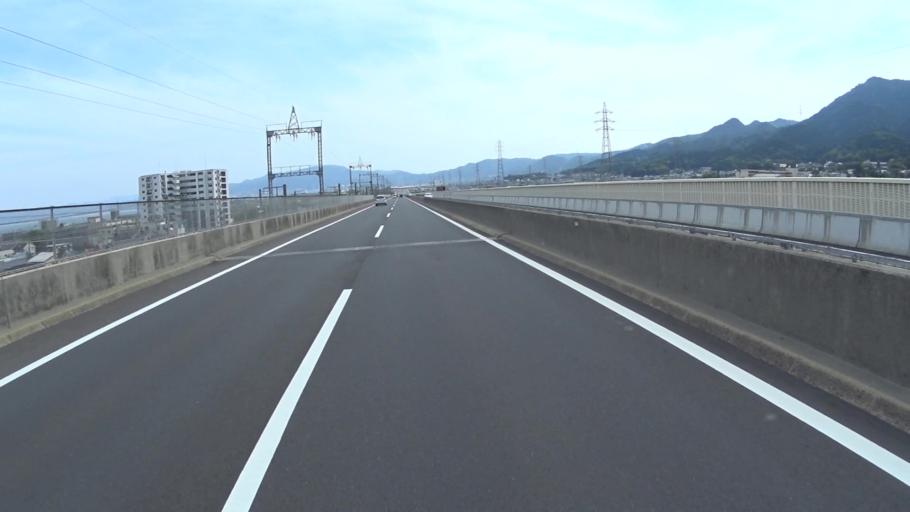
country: JP
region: Shiga Prefecture
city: Otsu-shi
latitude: 35.0725
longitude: 135.8791
